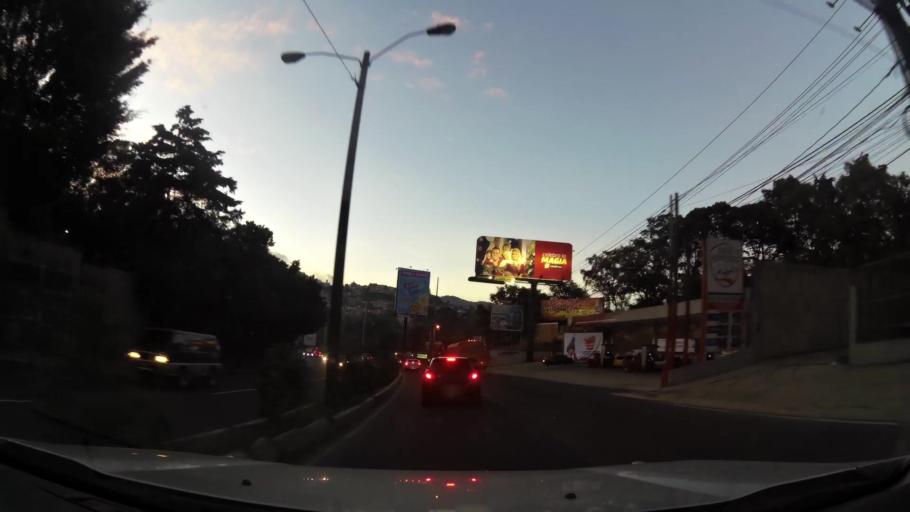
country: GT
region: Guatemala
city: Mixco
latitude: 14.6239
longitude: -90.6050
